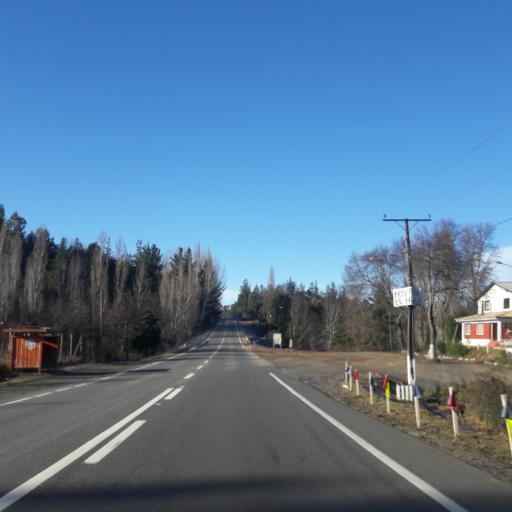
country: CL
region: Biobio
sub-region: Provincia de Biobio
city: La Laja
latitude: -37.3245
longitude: -72.9159
